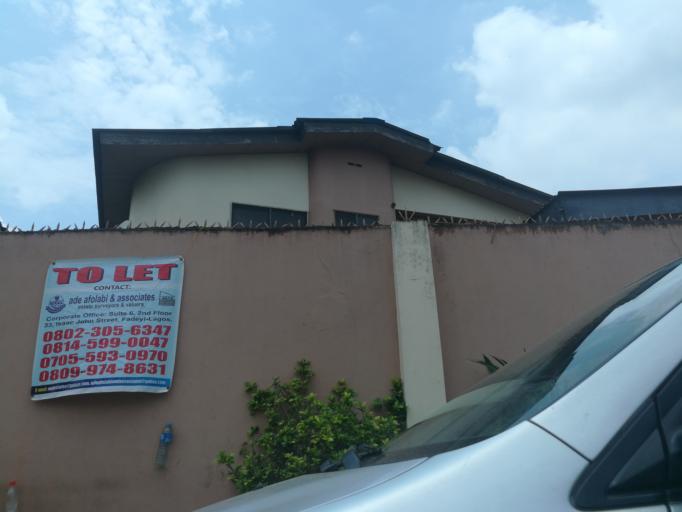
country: NG
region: Lagos
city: Ikeja
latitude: 6.5949
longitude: 3.3596
